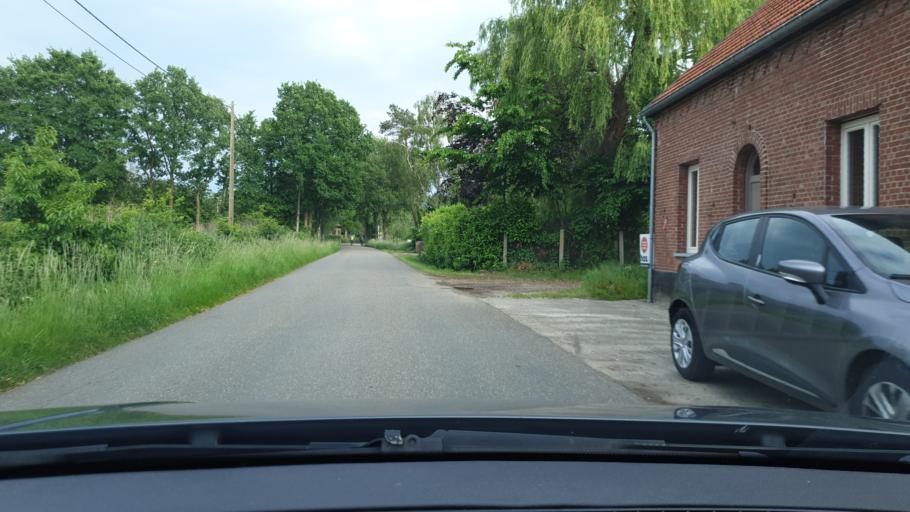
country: BE
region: Flanders
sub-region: Provincie Antwerpen
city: Geel
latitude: 51.1344
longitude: 4.9744
